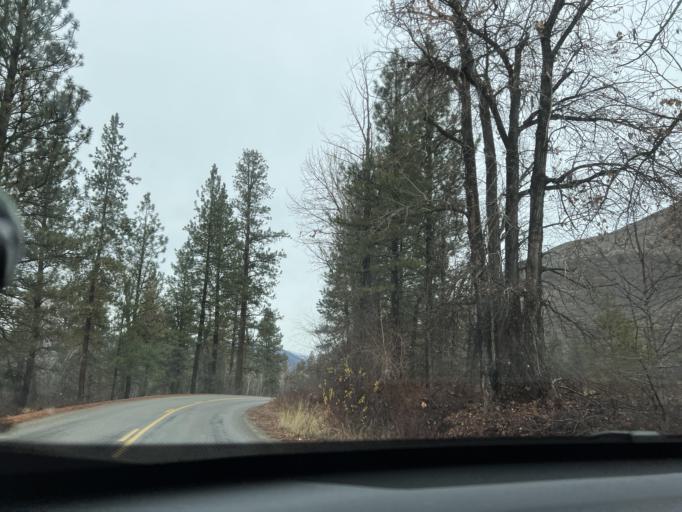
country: US
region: Washington
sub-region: Okanogan County
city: Brewster
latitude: 48.5289
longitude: -120.1803
